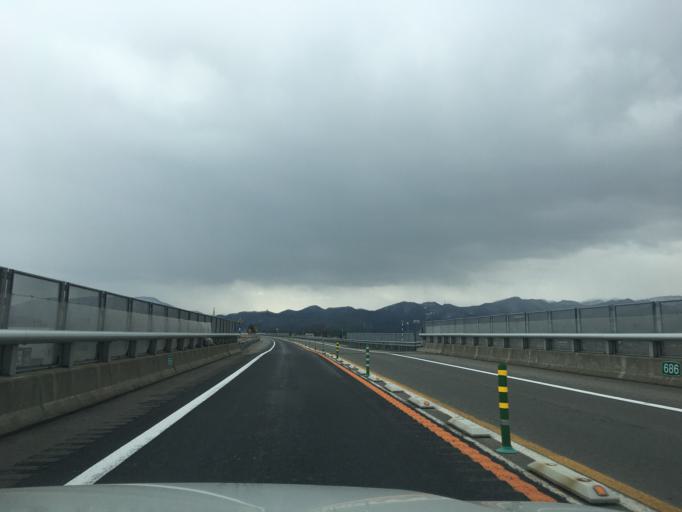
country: JP
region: Aomori
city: Aomori Shi
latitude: 40.7957
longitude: 140.7726
